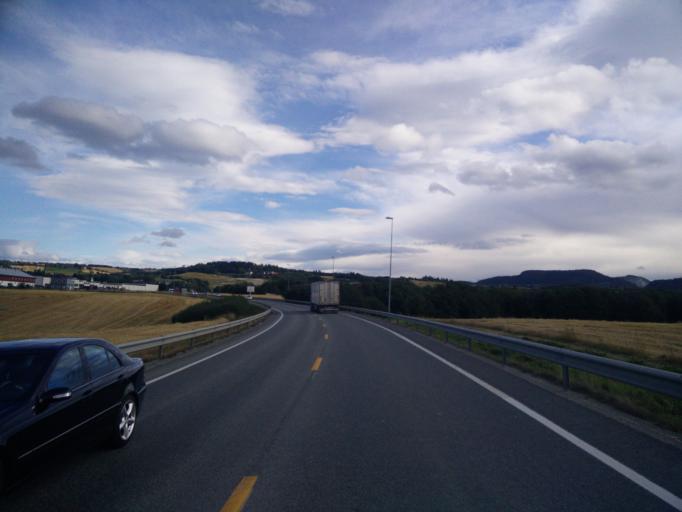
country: NO
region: Sor-Trondelag
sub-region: Melhus
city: Melhus
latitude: 63.3221
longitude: 10.3140
